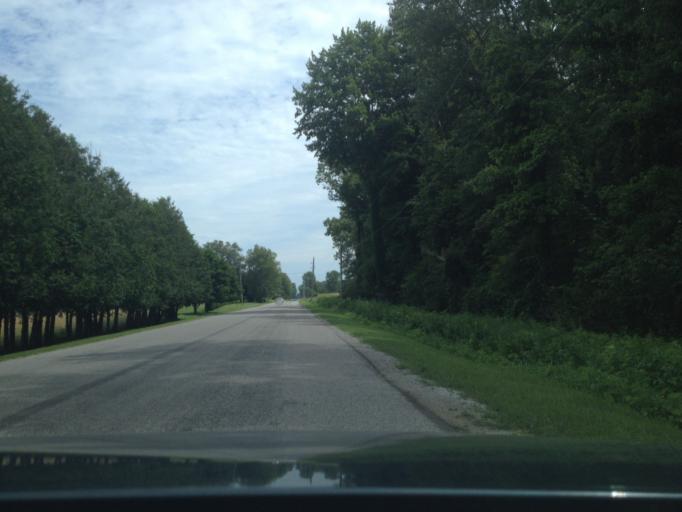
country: CA
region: Ontario
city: Norfolk County
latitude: 42.8533
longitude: -80.4122
